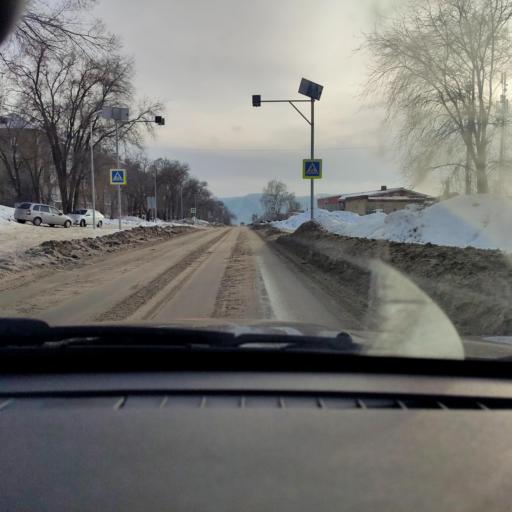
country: RU
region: Samara
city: Pribrezhnyy
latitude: 53.4885
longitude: 49.8469
